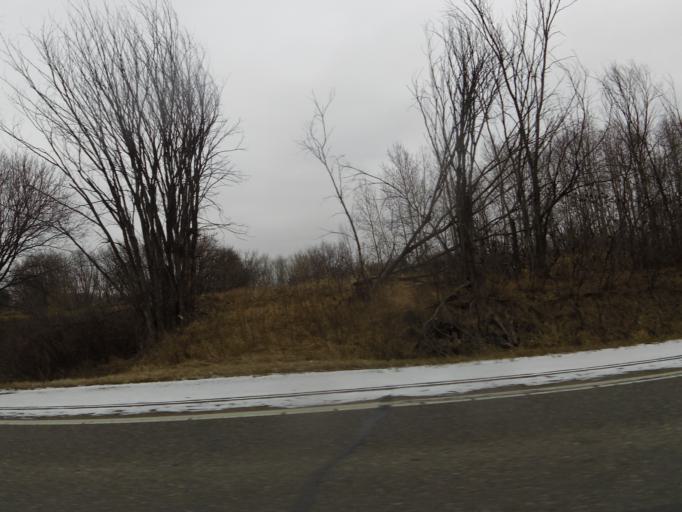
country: US
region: Minnesota
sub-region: Hennepin County
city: Independence
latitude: 45.0268
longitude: -93.7163
